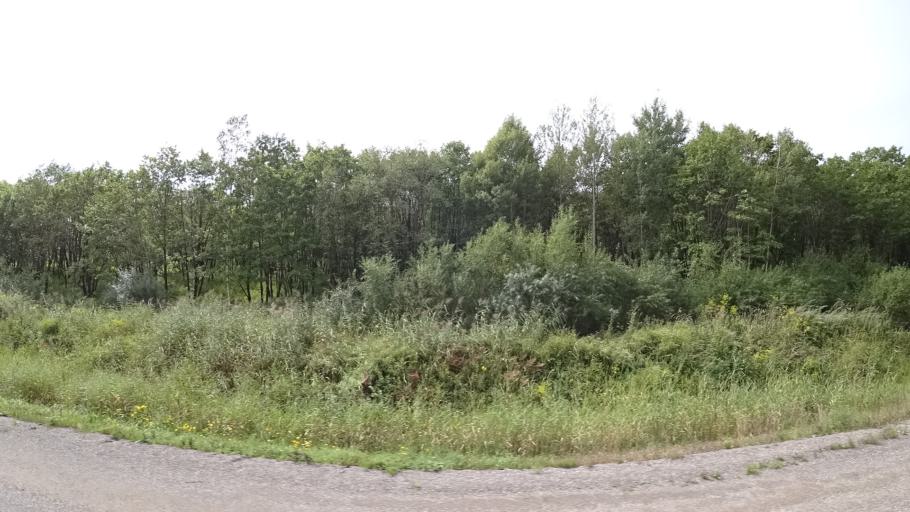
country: RU
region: Primorskiy
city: Lyalichi
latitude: 44.1132
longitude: 132.4196
